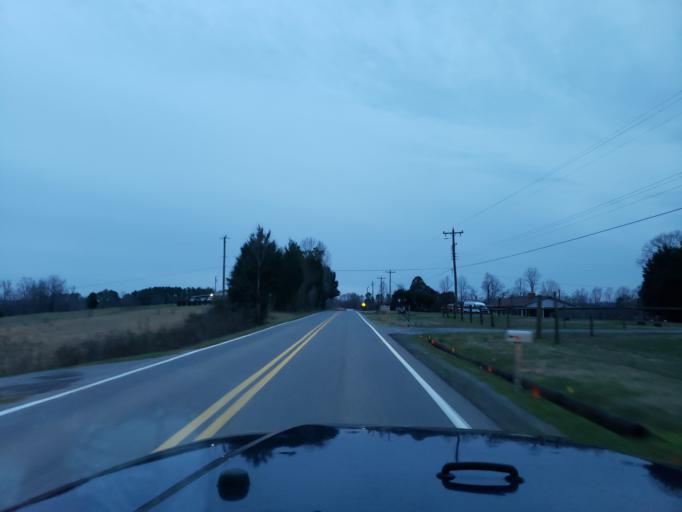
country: US
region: North Carolina
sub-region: Cleveland County
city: White Plains
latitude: 35.2326
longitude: -81.4586
